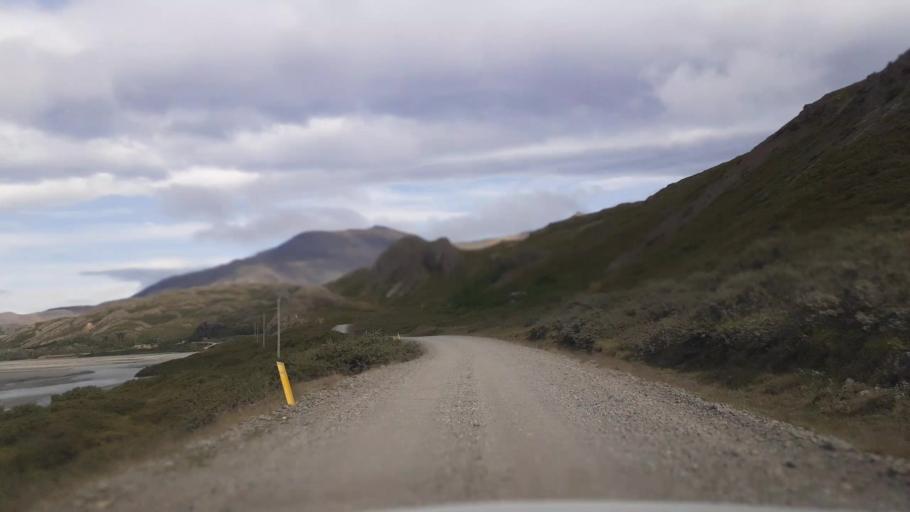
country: IS
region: East
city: Hoefn
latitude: 64.4259
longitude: -14.8827
